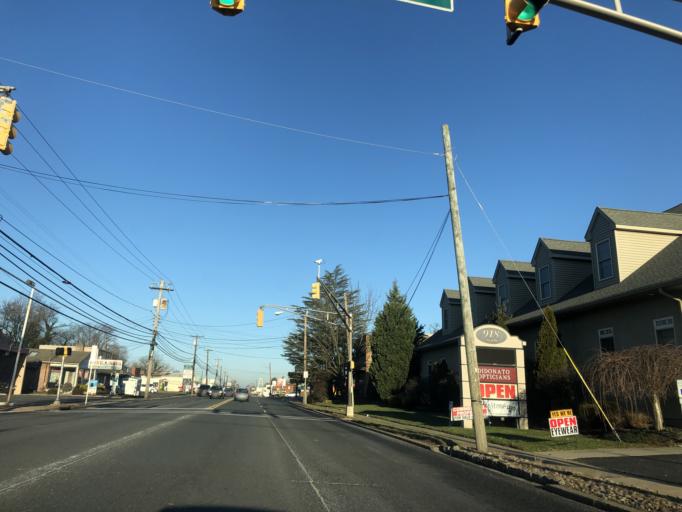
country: US
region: New Jersey
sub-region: Camden County
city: Stratford
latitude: 39.8366
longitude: -75.0085
